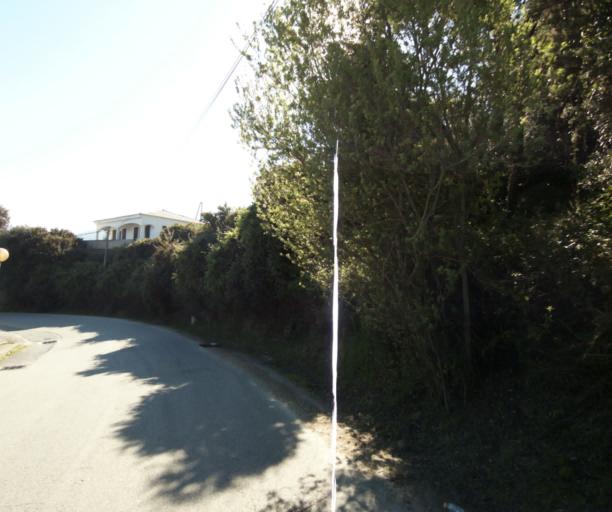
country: FR
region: Corsica
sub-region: Departement de la Corse-du-Sud
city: Propriano
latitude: 41.6700
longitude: 8.9055
